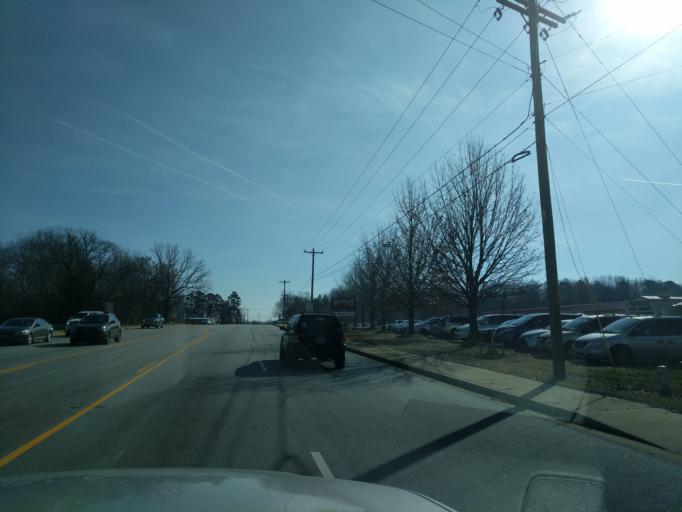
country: US
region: South Carolina
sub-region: Spartanburg County
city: Duncan
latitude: 34.8831
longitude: -82.1501
